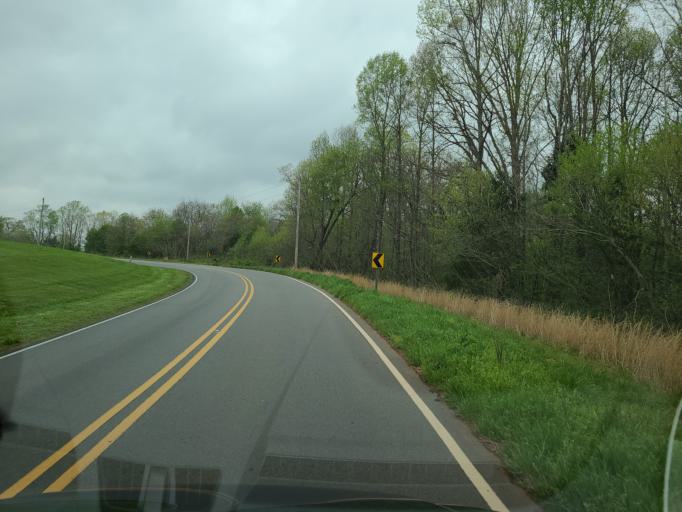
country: US
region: North Carolina
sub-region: Lincoln County
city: Lincolnton
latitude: 35.4571
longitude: -81.3376
